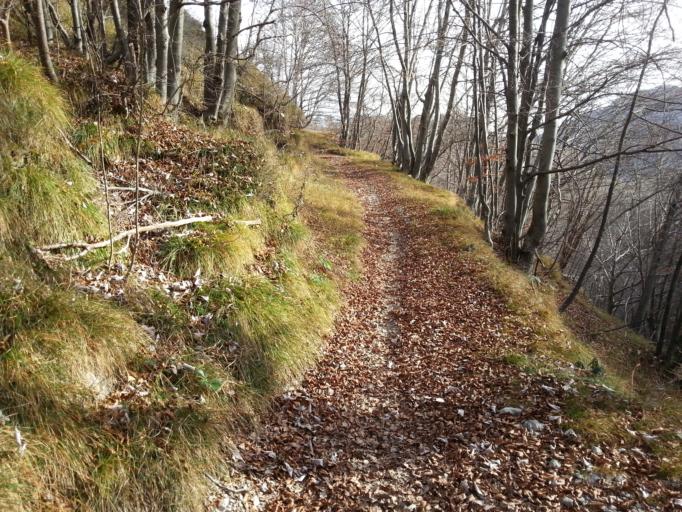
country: IT
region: Lombardy
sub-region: Provincia di Lecco
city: Morterone
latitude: 45.8887
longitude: 9.4773
